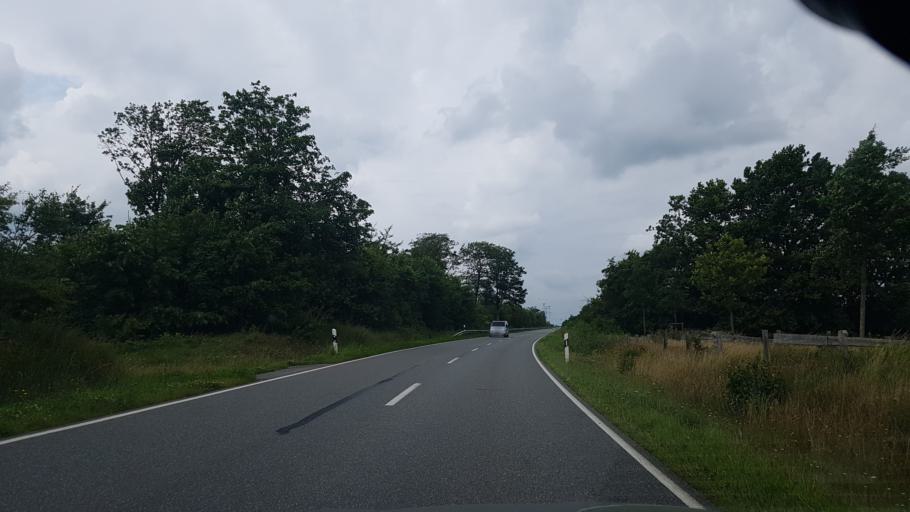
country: DE
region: Schleswig-Holstein
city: Osterby
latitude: 54.8200
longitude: 9.2230
